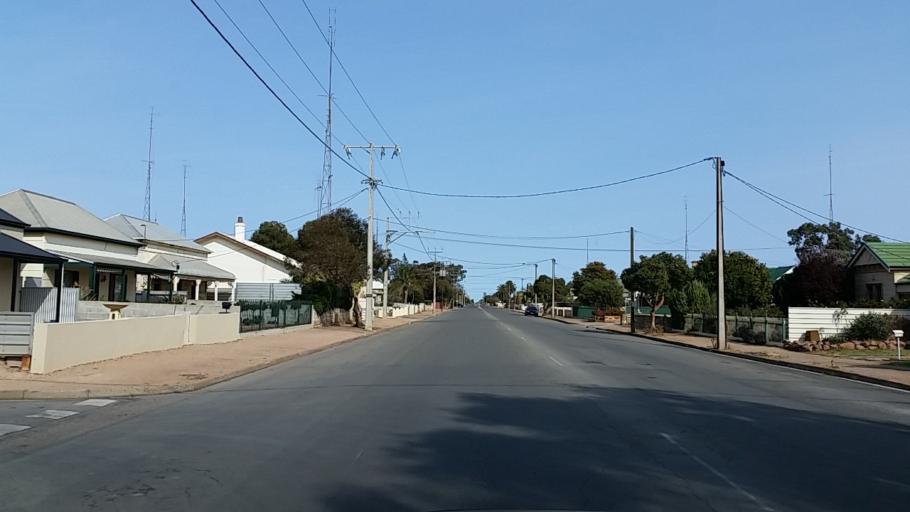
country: AU
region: South Australia
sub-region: Port Pirie City and Dists
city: Port Pirie
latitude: -33.1813
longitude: 138.0004
